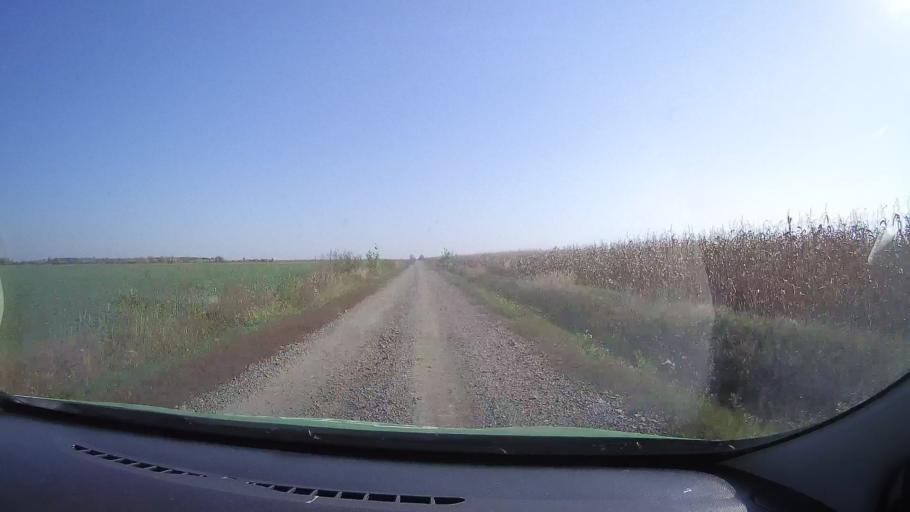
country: RO
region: Satu Mare
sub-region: Comuna Urziceni
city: Urziceni
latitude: 47.7356
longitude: 22.4127
